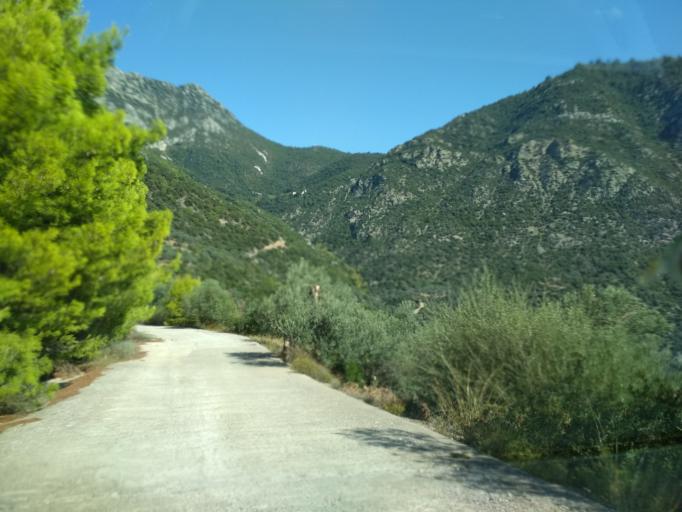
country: GR
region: Central Greece
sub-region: Nomos Evvoias
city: Oreoi
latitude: 38.8519
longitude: 23.1159
